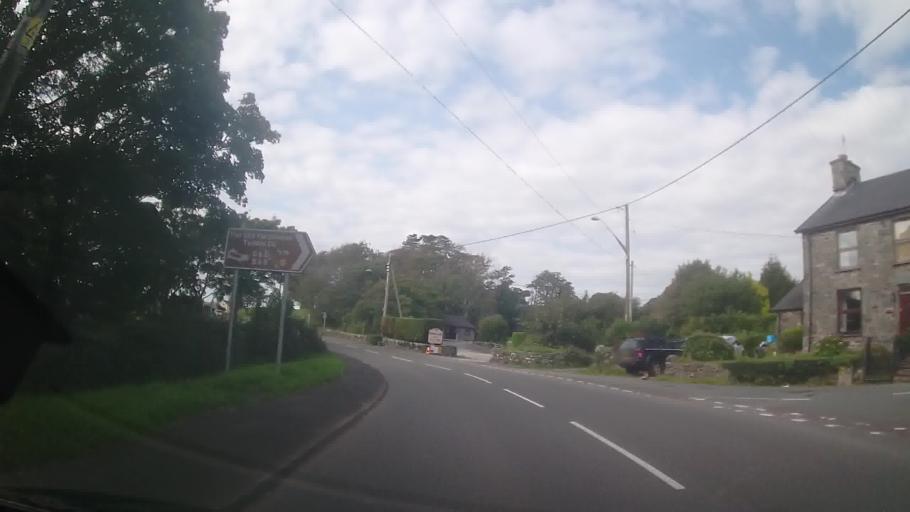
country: GB
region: Wales
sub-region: Gwynedd
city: Llanbedr
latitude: 52.7896
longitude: -4.0972
